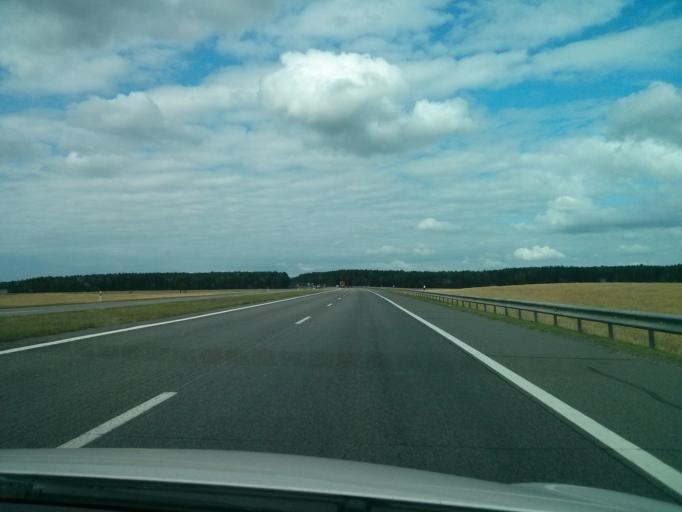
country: BY
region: Minsk
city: Zamostochcha
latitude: 53.8819
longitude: 27.9356
